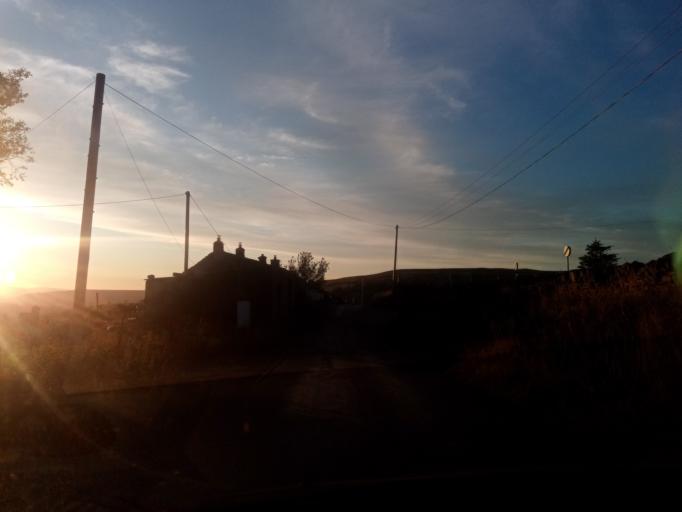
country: GB
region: England
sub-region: Northumberland
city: Bardon Mill
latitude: 54.7913
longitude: -2.3415
